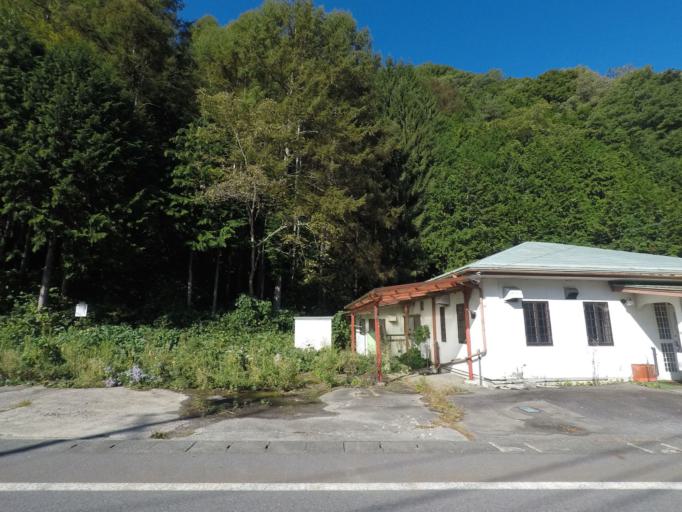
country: JP
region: Nagano
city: Ina
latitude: 35.9630
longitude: 137.7664
